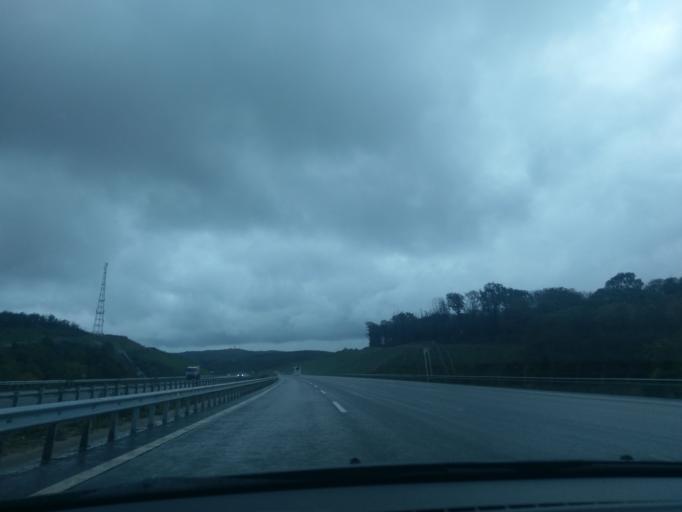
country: TR
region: Istanbul
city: Kemerburgaz
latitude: 41.2312
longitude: 28.9299
